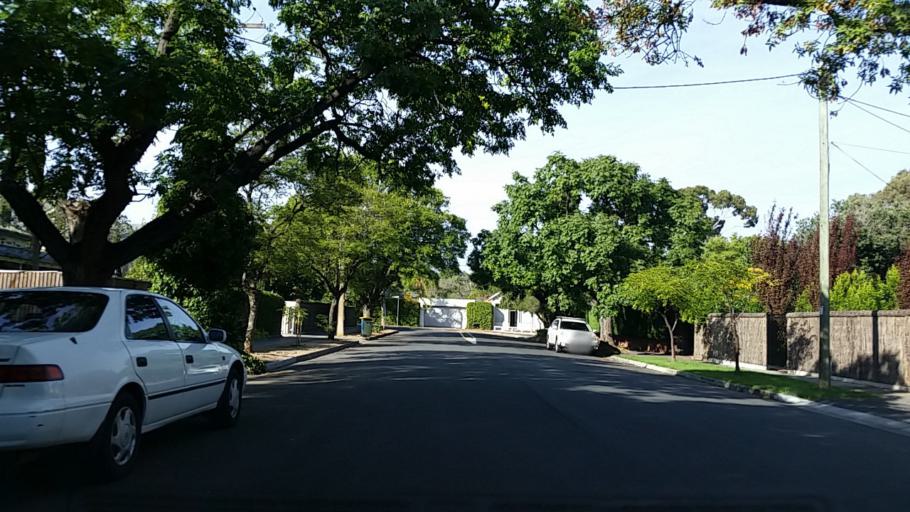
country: AU
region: South Australia
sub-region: Mitcham
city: Hawthorn
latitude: -34.9691
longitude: 138.6012
